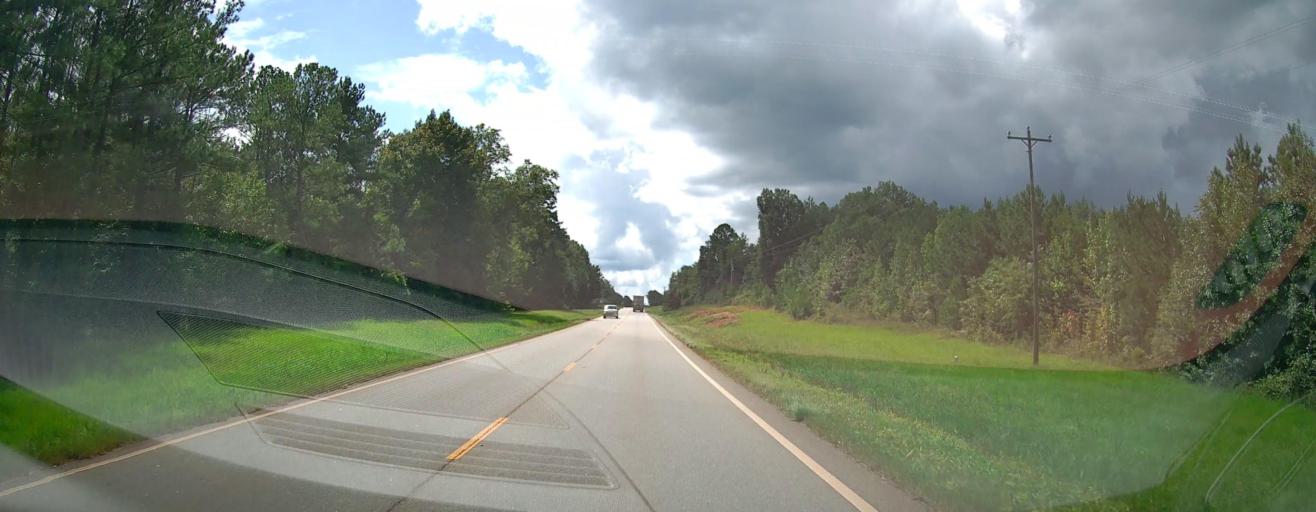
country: US
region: Georgia
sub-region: Bibb County
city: West Point
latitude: 32.8646
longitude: -83.8581
